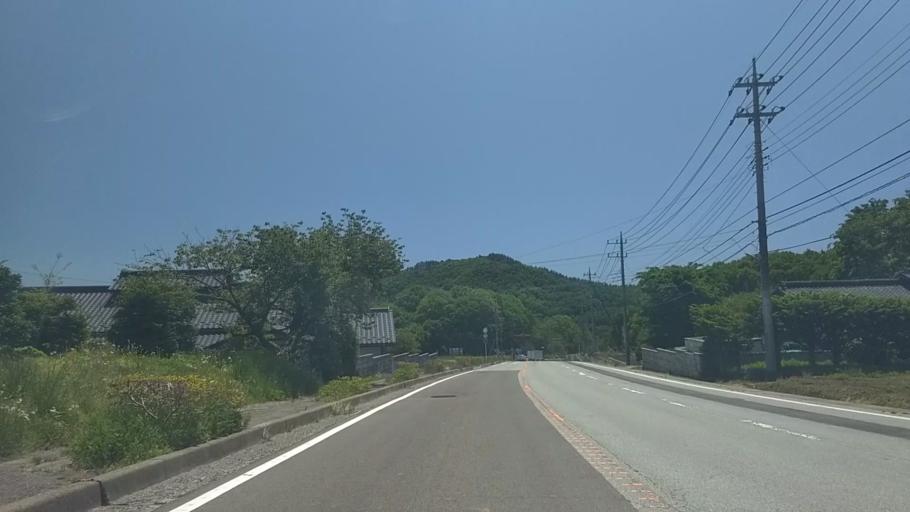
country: JP
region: Yamanashi
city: Nirasaki
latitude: 35.8806
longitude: 138.4398
